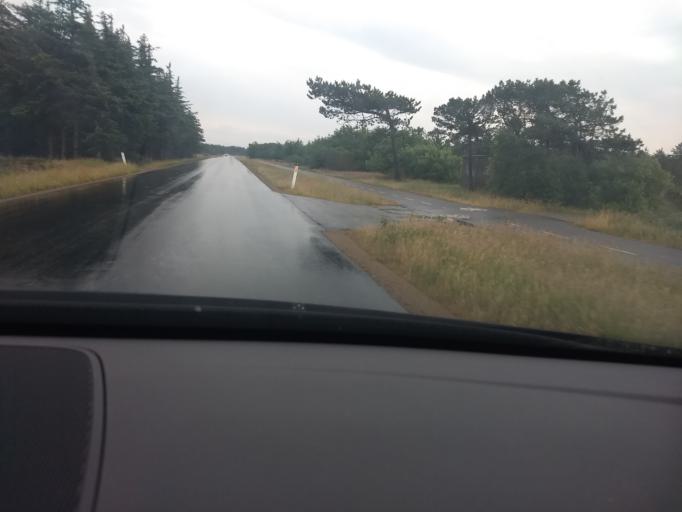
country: DK
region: South Denmark
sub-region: Fano Kommune
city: Nordby
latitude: 55.4084
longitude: 8.4139
